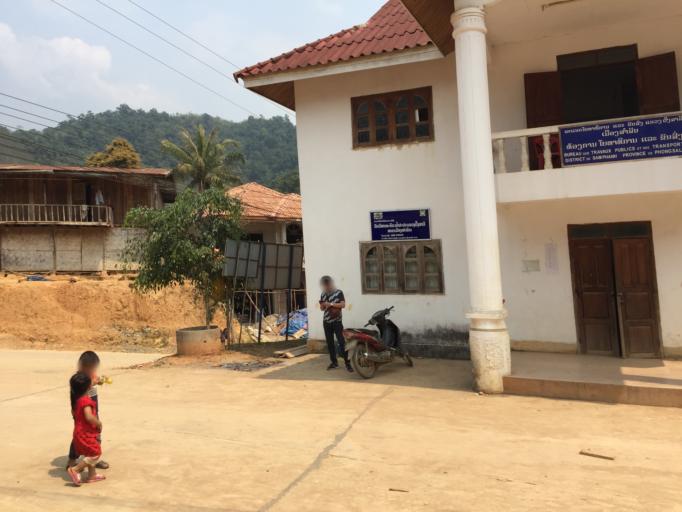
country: LA
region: Phongsali
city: Khoa
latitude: 21.3459
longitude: 102.3490
